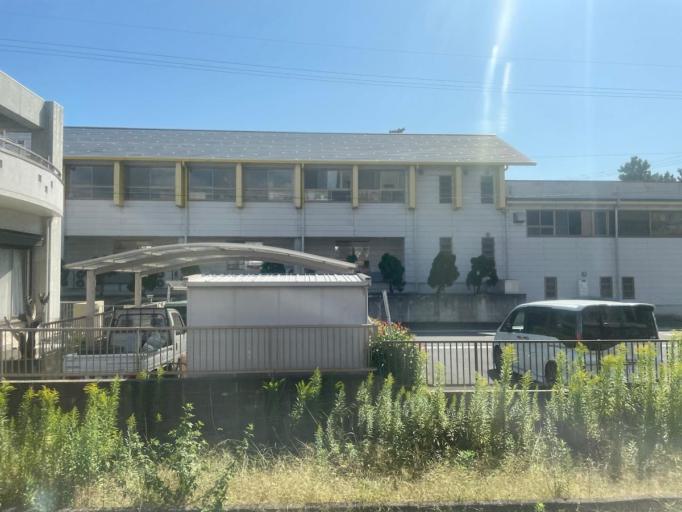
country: JP
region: Mie
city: Suzuka
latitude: 34.8351
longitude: 136.5909
